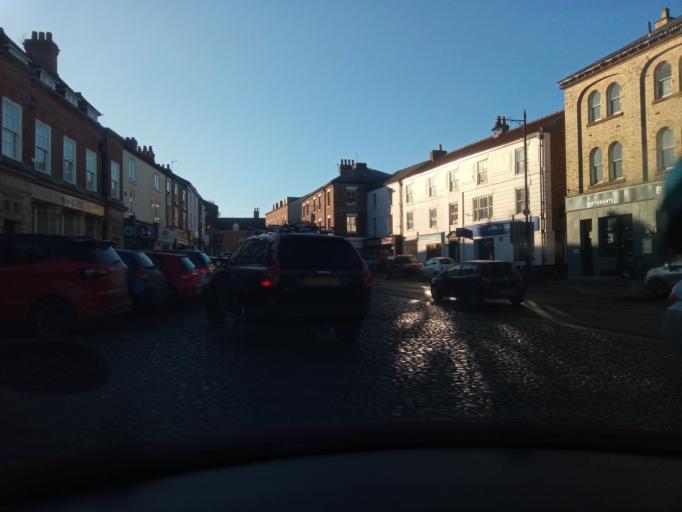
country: GB
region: England
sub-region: North Yorkshire
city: Thirsk
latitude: 54.2324
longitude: -1.3429
